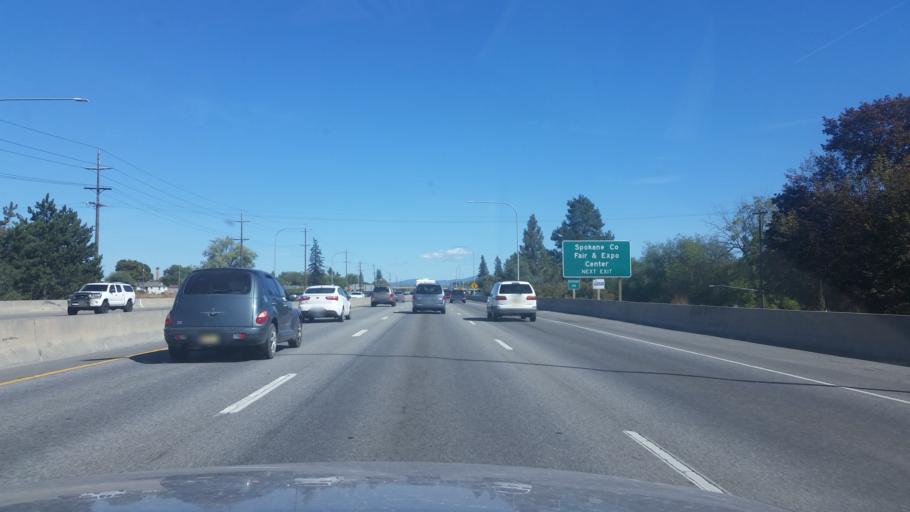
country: US
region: Washington
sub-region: Spokane County
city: Spokane
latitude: 47.6539
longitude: -117.3745
